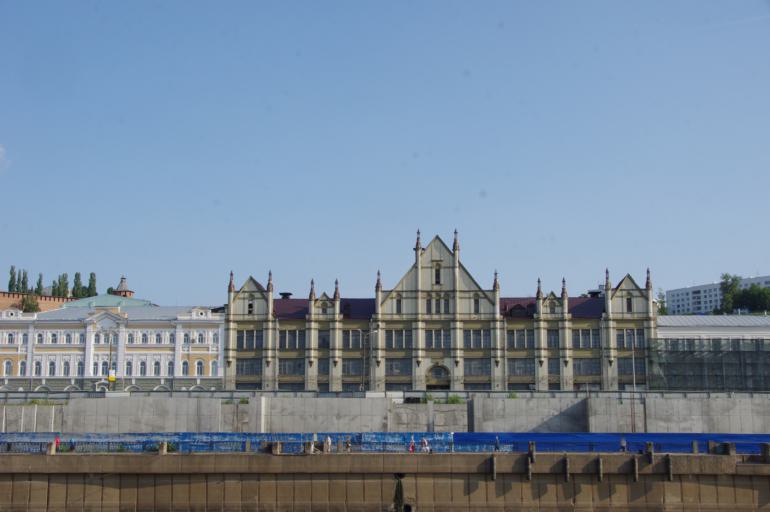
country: RU
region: Nizjnij Novgorod
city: Nizhniy Novgorod
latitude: 56.3318
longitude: 43.9919
